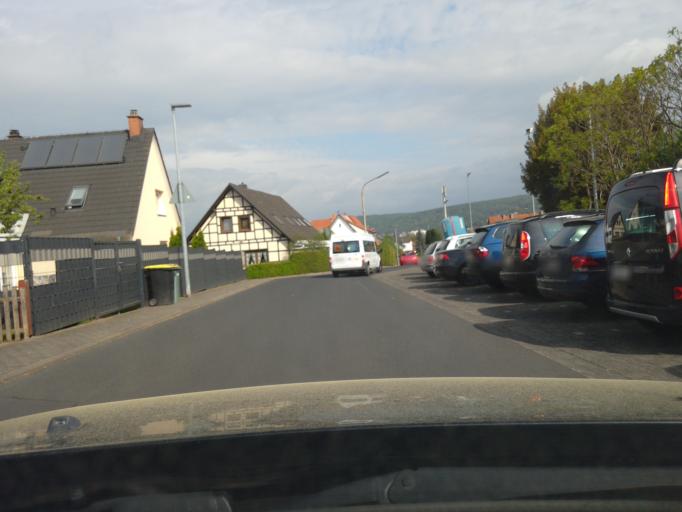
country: DE
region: Hesse
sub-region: Regierungsbezirk Darmstadt
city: Gelnhausen
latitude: 50.1841
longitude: 9.1969
